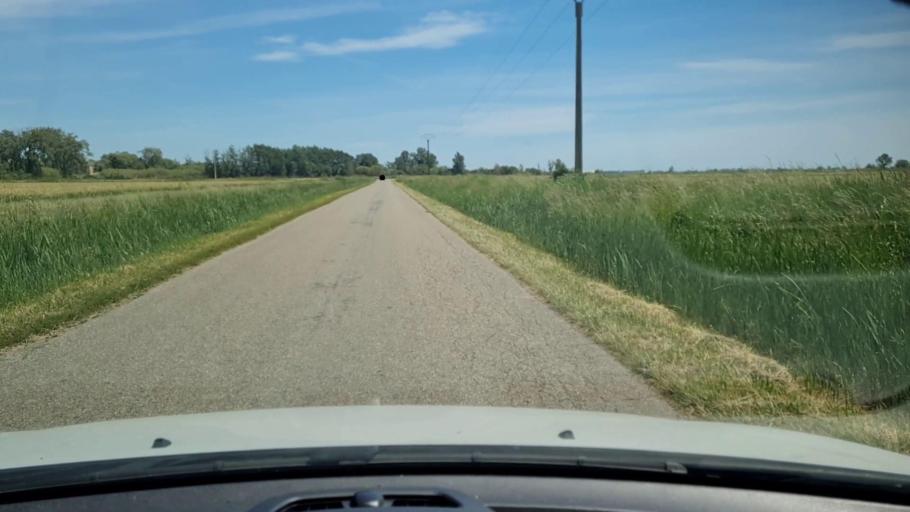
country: FR
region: Languedoc-Roussillon
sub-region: Departement du Gard
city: Saint-Gilles
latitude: 43.6208
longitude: 4.4233
